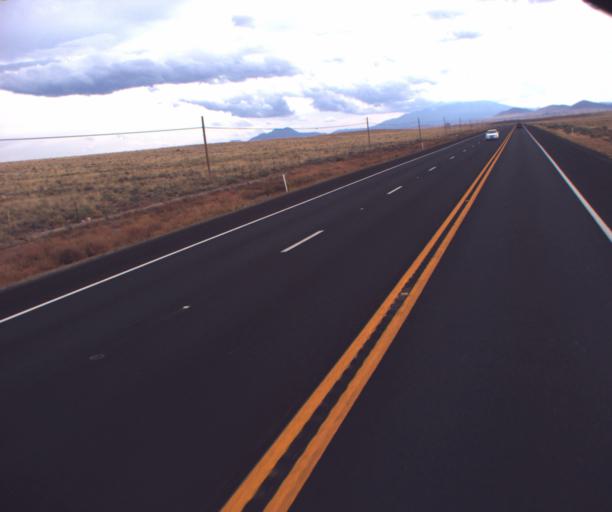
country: US
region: Arizona
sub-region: Coconino County
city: Tuba City
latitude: 35.6974
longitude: -111.5006
